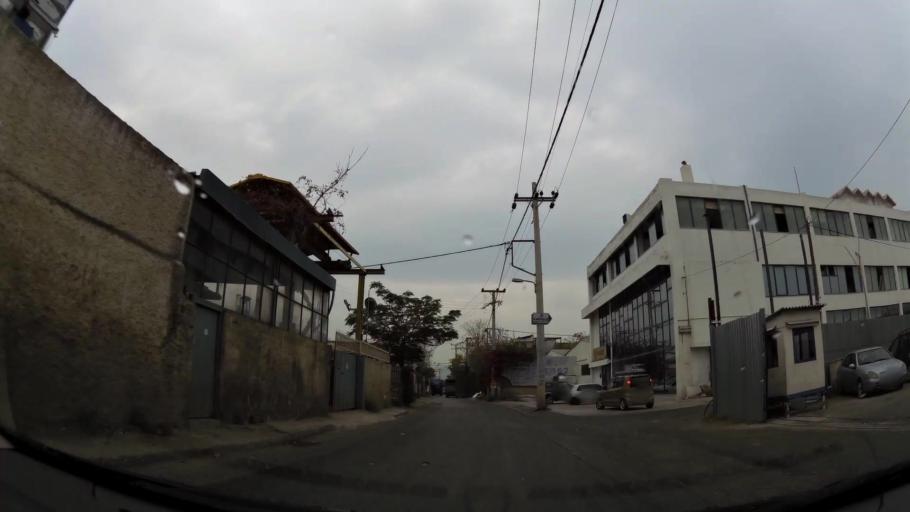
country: GR
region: Attica
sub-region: Nomarchia Athinas
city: Tavros
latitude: 37.9789
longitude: 23.6962
